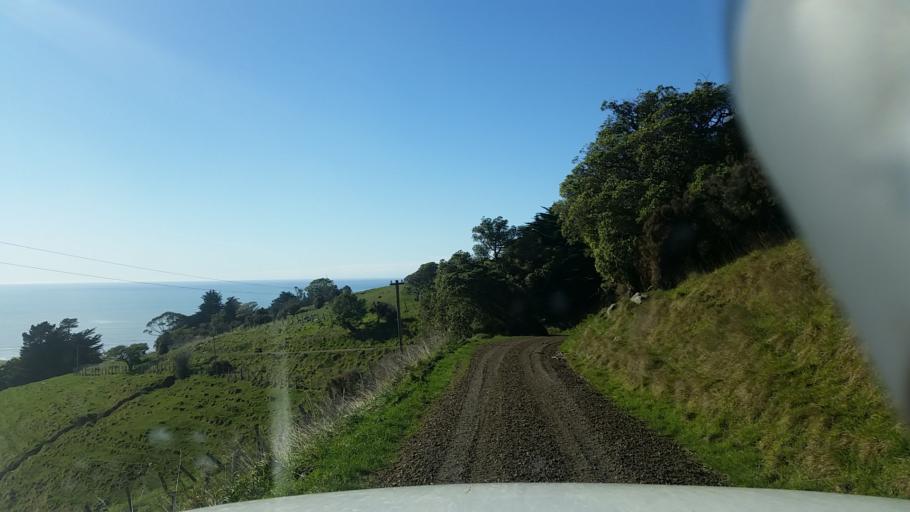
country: NZ
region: Canterbury
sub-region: Christchurch City
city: Christchurch
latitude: -43.6700
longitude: 173.0231
